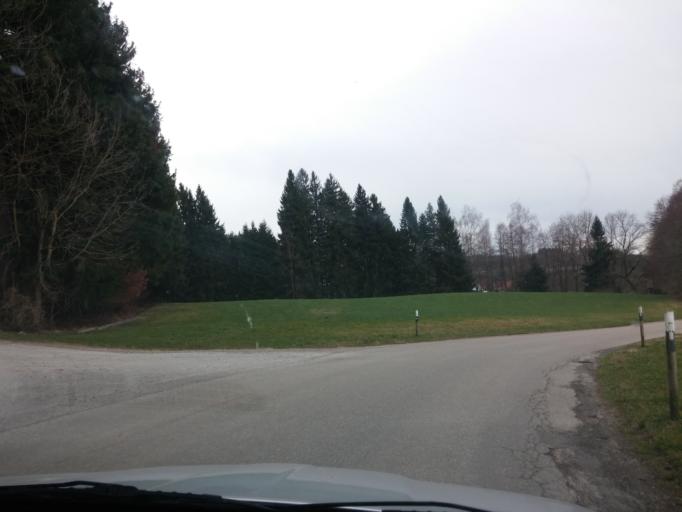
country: DE
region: Bavaria
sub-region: Swabia
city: Woringen
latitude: 47.9122
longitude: 10.1833
